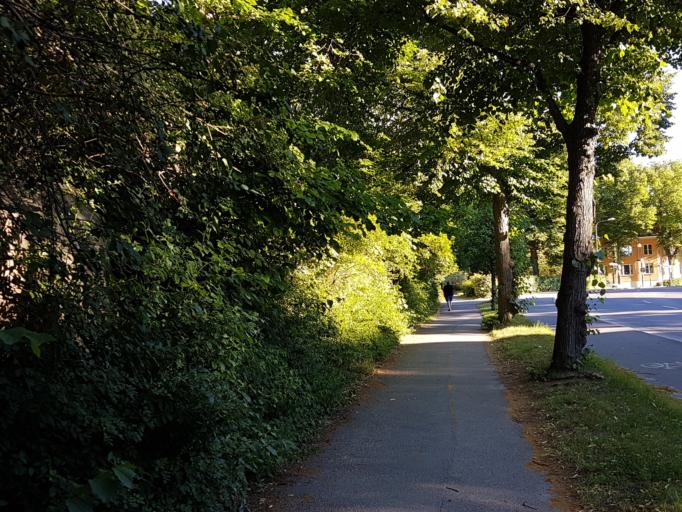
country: SE
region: Stockholm
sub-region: Sundbybergs Kommun
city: Sundbyberg
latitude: 59.3304
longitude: 17.9754
